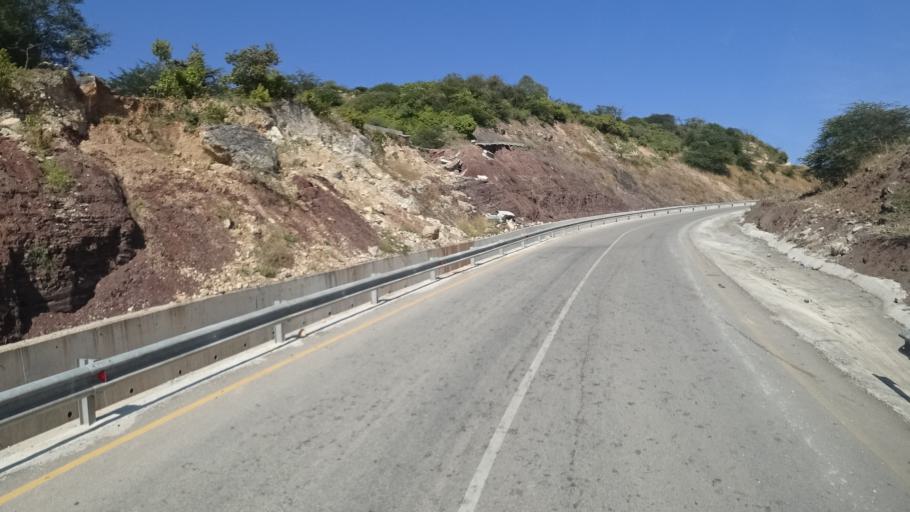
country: OM
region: Zufar
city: Salalah
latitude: 17.0525
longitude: 54.6105
